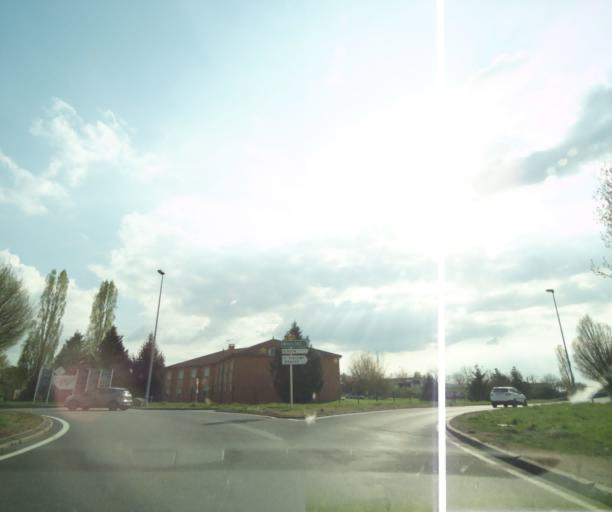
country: FR
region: Bourgogne
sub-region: Departement de Saone-et-Loire
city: Paray-le-Monial
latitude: 46.4684
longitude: 4.1182
